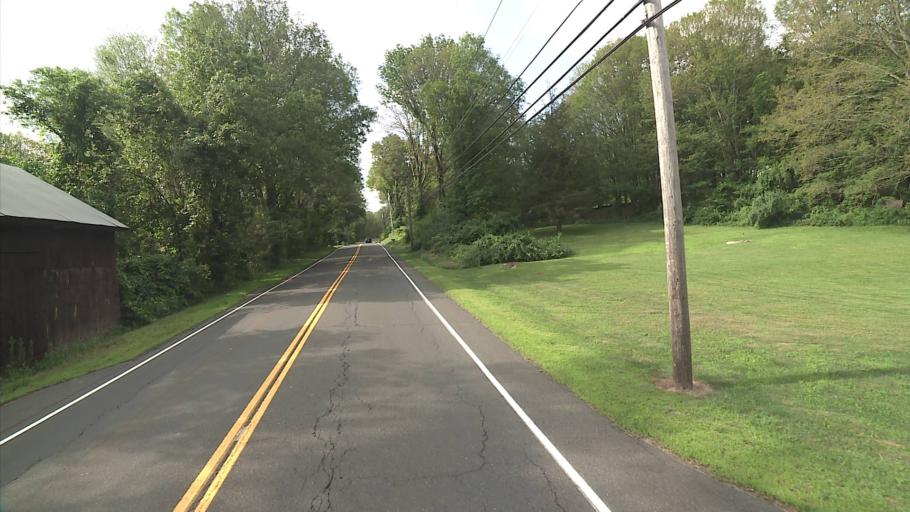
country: US
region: Connecticut
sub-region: Middlesex County
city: Higganum
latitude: 41.4625
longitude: -72.5557
